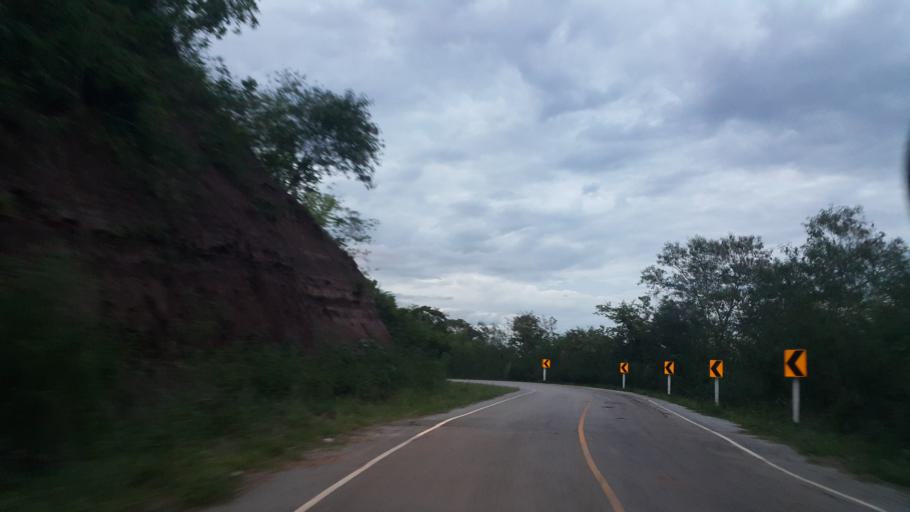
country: TH
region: Loei
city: Phu Ruea
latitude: 17.5137
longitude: 101.2319
